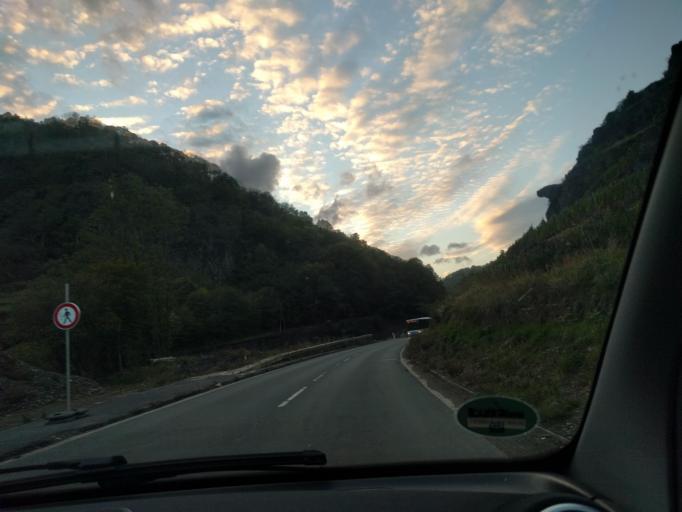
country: DE
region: Rheinland-Pfalz
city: Dernau
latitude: 50.5294
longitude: 7.0711
